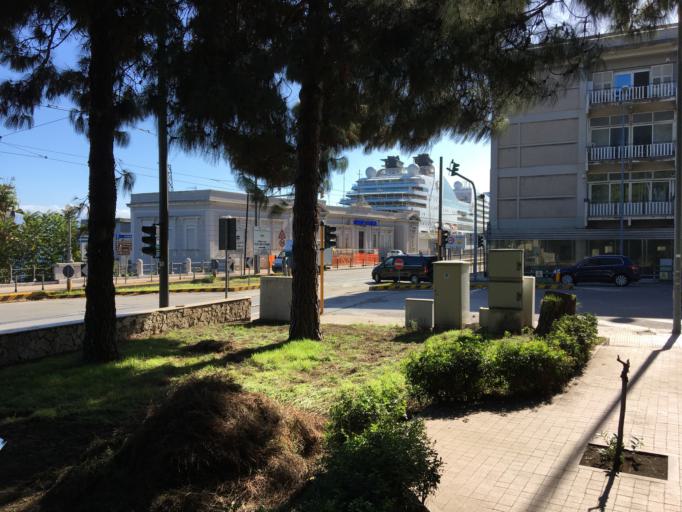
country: IT
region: Sicily
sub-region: Messina
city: Messina
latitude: 38.1974
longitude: 15.5575
